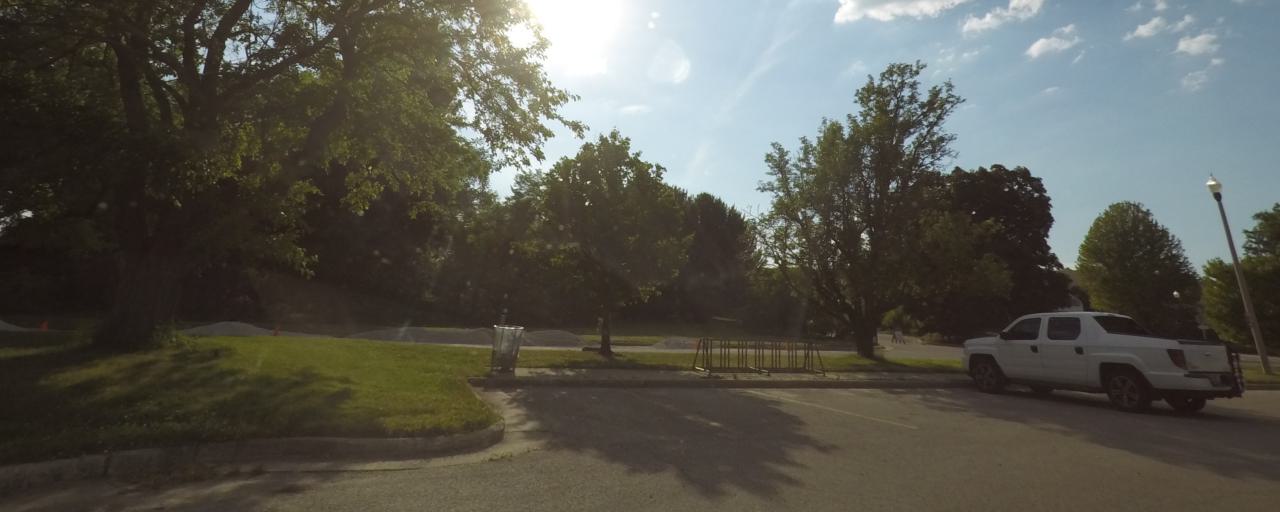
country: US
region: Wisconsin
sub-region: Milwaukee County
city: Hales Corners
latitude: 42.9363
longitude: -88.0300
